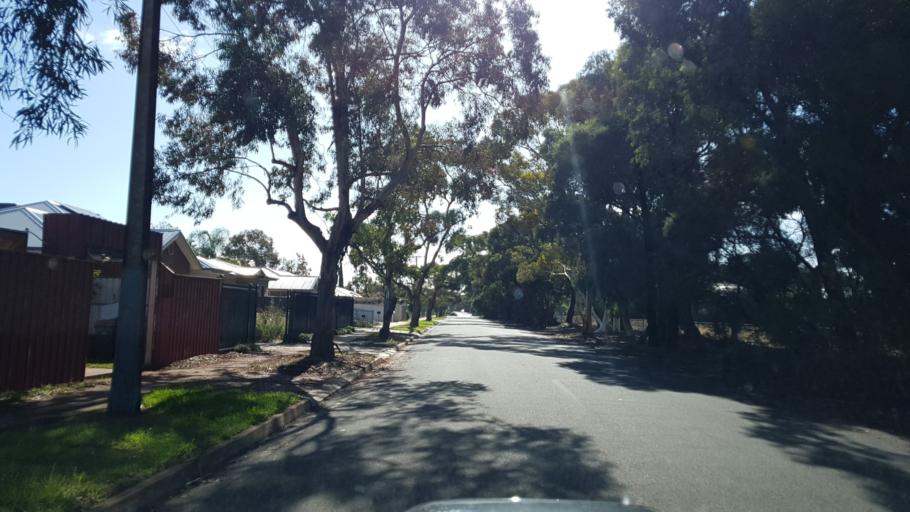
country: AU
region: South Australia
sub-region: Salisbury
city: Salisbury
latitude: -34.7503
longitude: 138.6394
